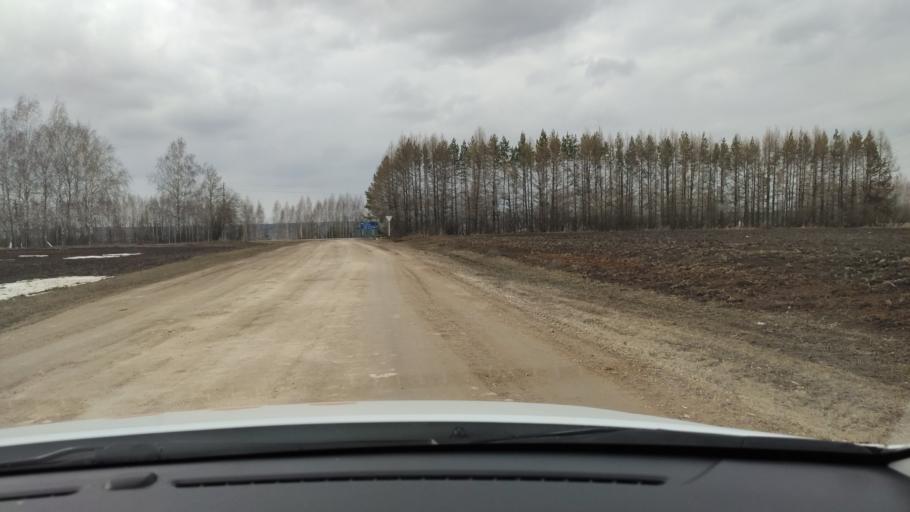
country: RU
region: Tatarstan
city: Vysokaya Gora
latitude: 56.2290
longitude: 49.3022
